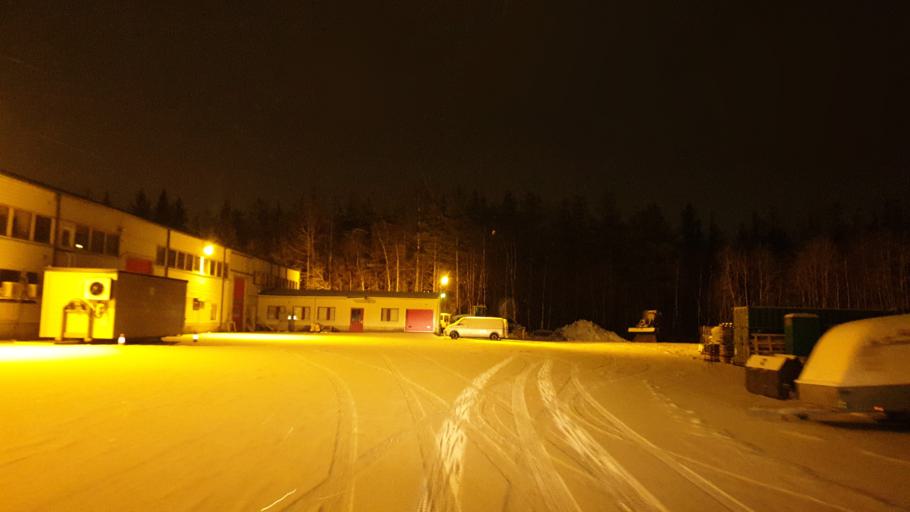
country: FI
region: Northern Ostrobothnia
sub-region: Oulu
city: Oulu
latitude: 64.9920
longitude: 25.4545
